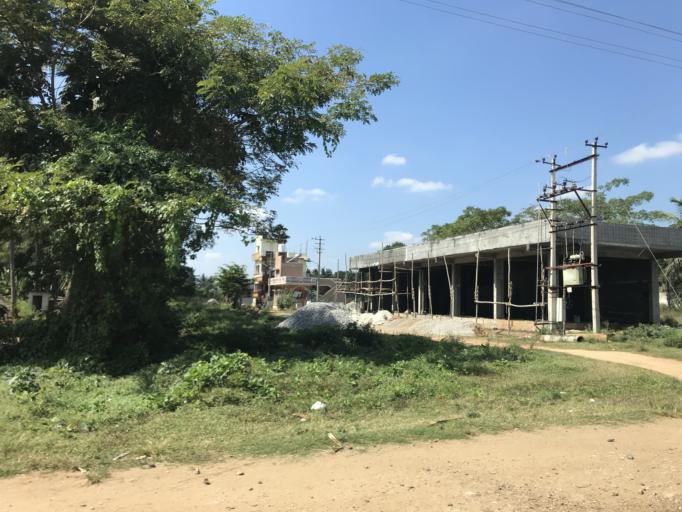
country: IN
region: Karnataka
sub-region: Mysore
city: Heggadadevankote
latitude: 12.0948
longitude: 76.3315
